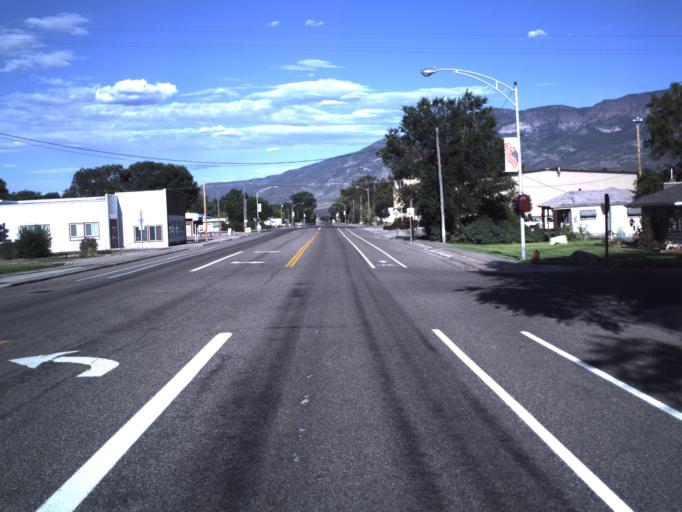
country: US
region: Utah
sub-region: Sevier County
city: Monroe
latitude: 38.6830
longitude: -112.1510
